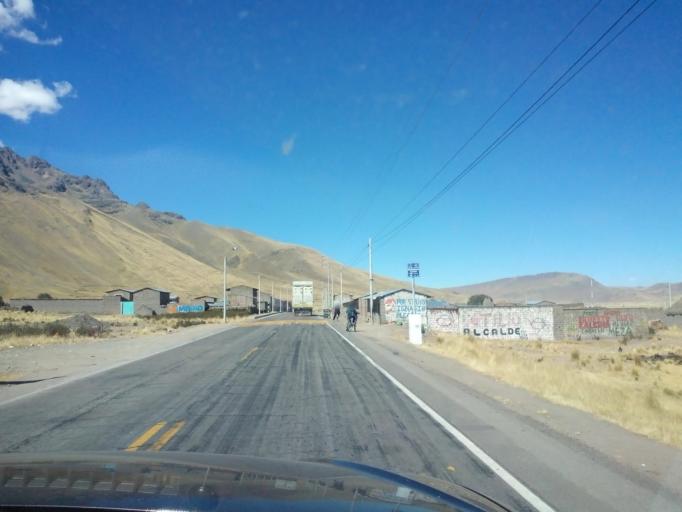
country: PE
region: Puno
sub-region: Provincia de Melgar
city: Santa Rosa
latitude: -14.5351
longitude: -70.8865
